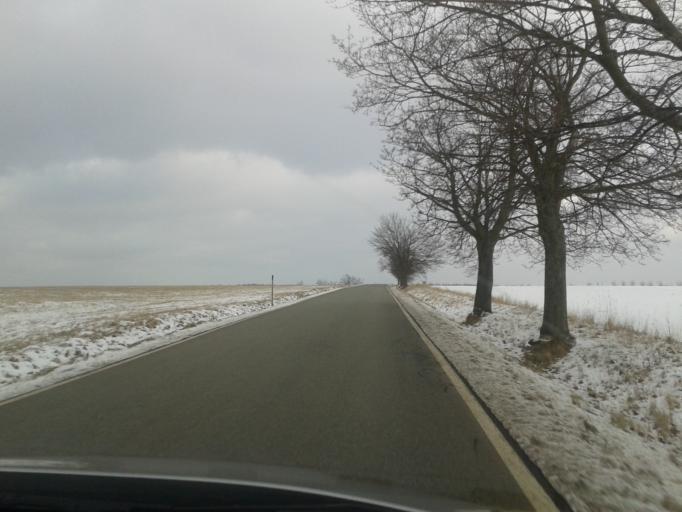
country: CZ
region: Olomoucky
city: Horni Stepanov
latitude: 49.5788
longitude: 16.8289
